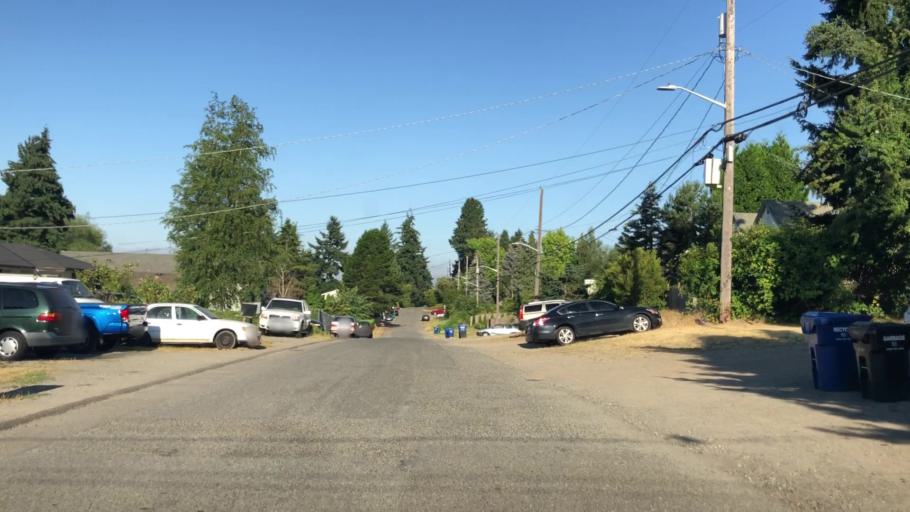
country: US
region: Washington
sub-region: King County
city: Bryn Mawr-Skyway
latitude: 47.4956
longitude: -122.2604
